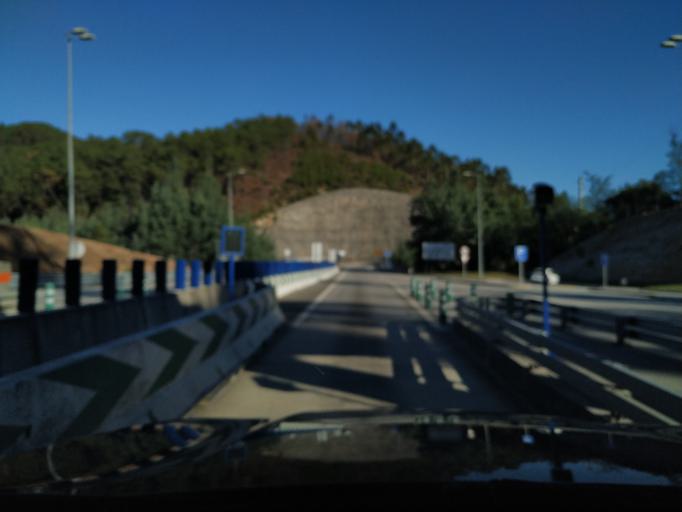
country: PT
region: Aveiro
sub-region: Oliveira de Azemeis
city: Vila Cha
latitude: 40.8770
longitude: -8.4294
